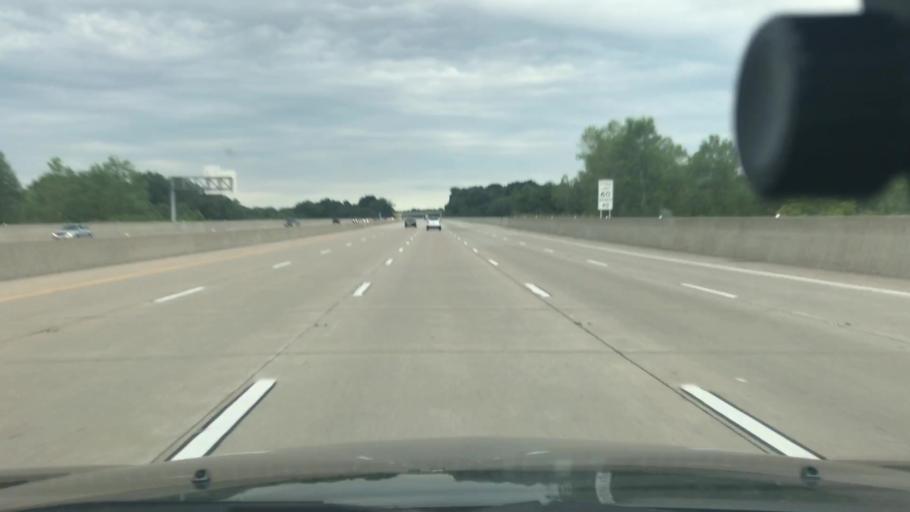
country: US
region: Missouri
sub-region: Saint Louis County
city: Maryland Heights
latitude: 38.7063
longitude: -90.4926
